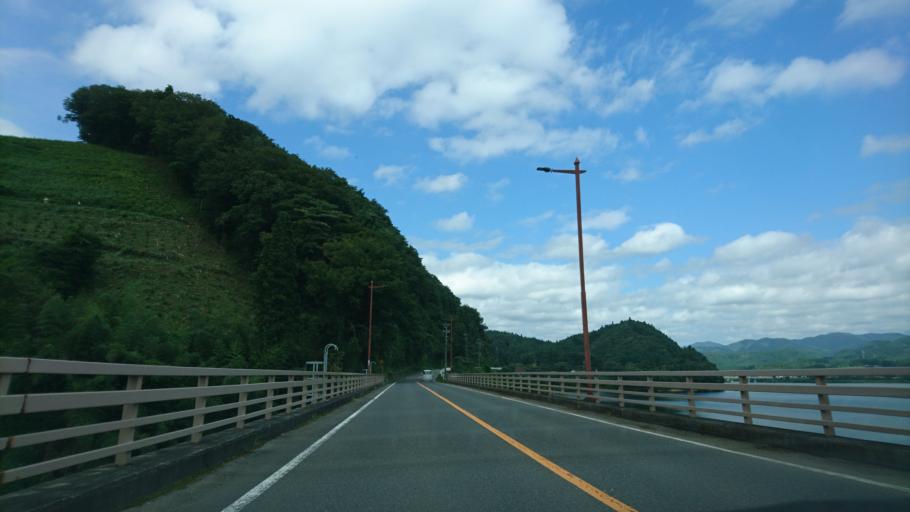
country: JP
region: Miyagi
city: Furukawa
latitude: 38.7757
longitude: 140.8566
